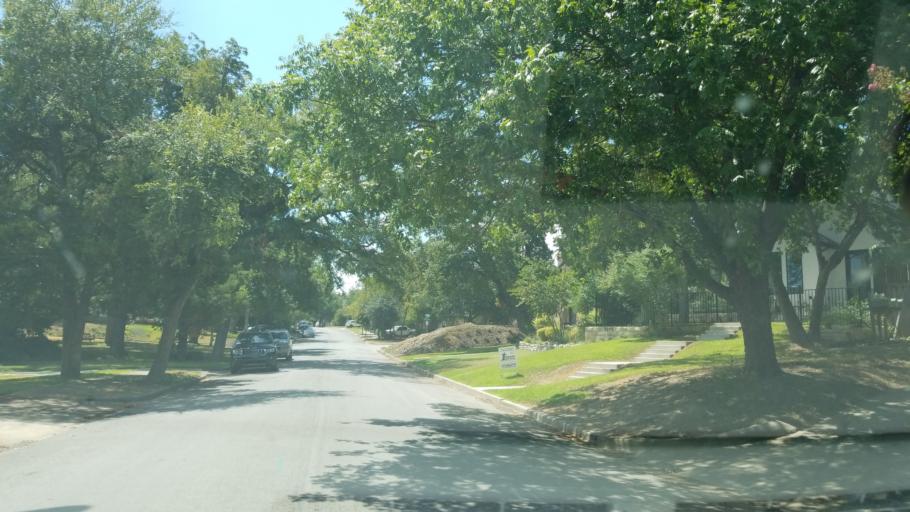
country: US
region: Texas
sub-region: Dallas County
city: Dallas
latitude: 32.7583
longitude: -96.8293
